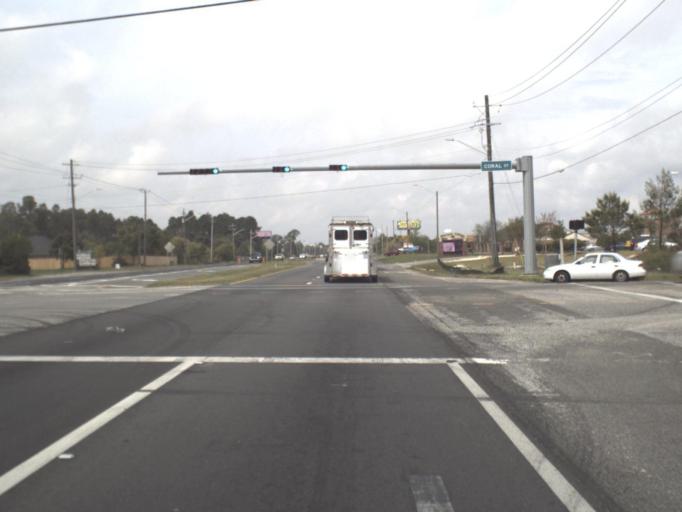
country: US
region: Florida
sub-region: Santa Rosa County
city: Navarre
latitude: 30.4020
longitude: -86.9050
